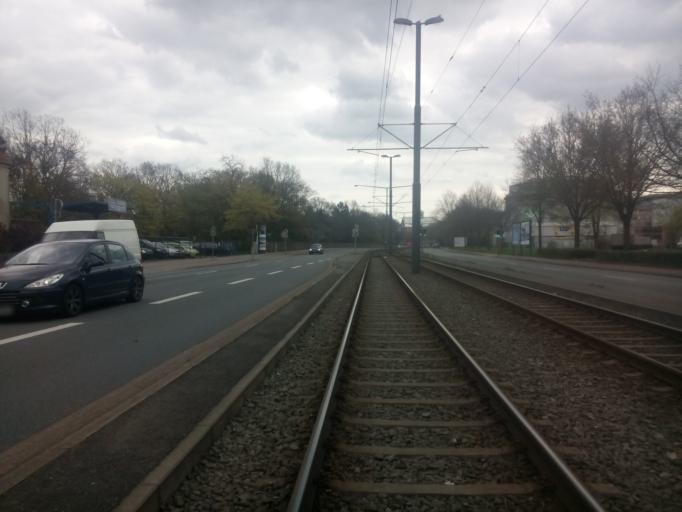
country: DE
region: Bremen
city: Bremen
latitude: 53.1075
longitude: 8.7652
